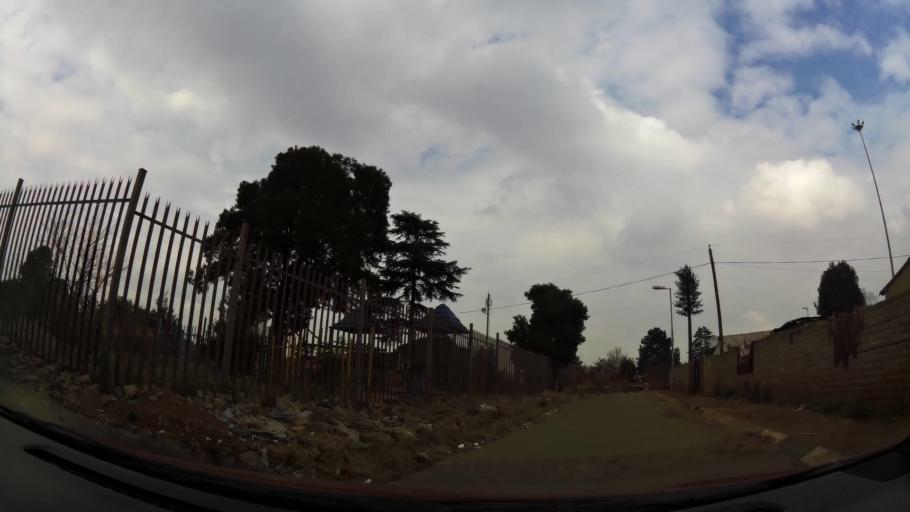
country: ZA
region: Gauteng
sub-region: City of Johannesburg Metropolitan Municipality
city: Soweto
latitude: -26.2538
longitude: 27.8254
